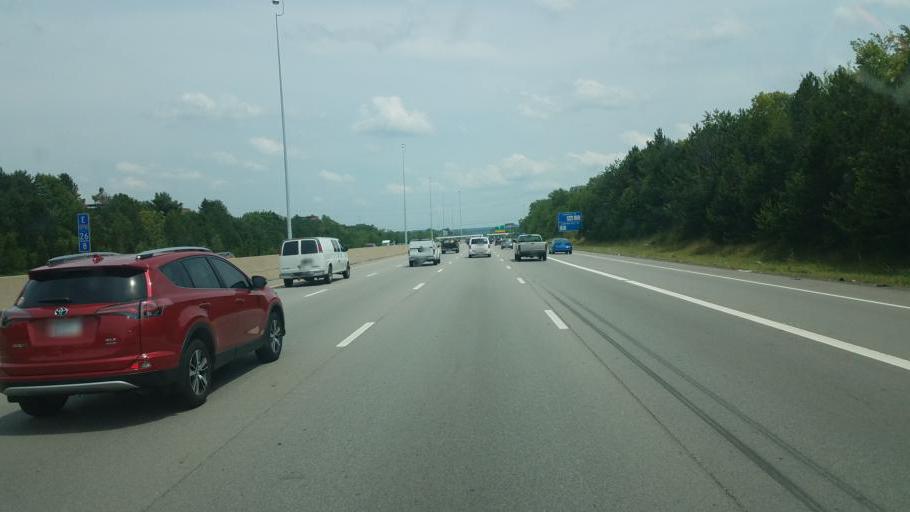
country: US
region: Ohio
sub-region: Franklin County
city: Minerva Park
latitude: 40.1076
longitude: -82.9610
